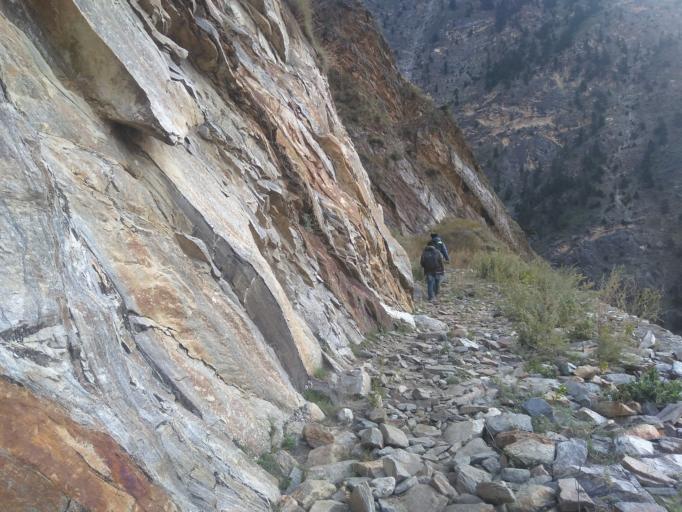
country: NP
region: Western Region
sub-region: Dhawalagiri Zone
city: Jomsom
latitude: 28.9035
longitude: 83.0287
